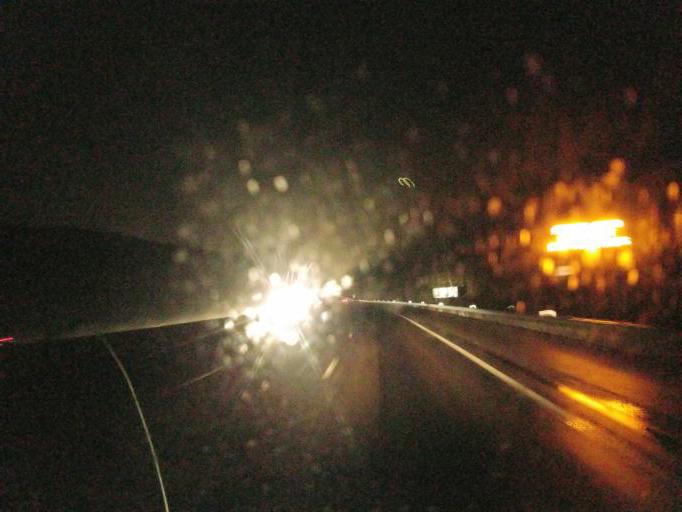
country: US
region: Missouri
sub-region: Franklin County
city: Pacific
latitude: 38.5018
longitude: -90.7057
